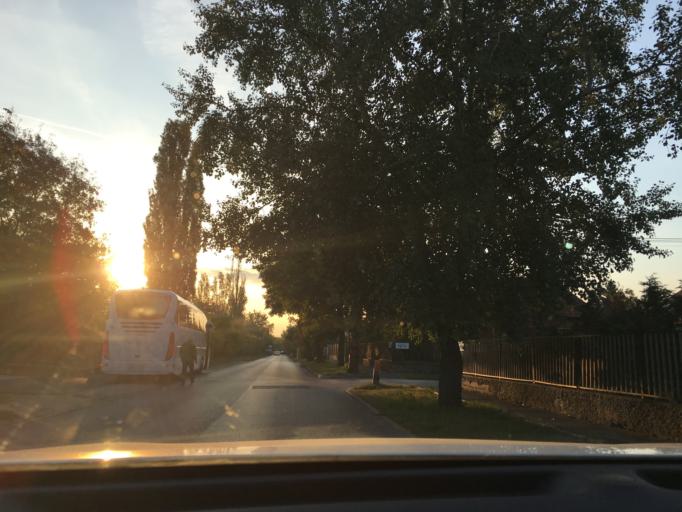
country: HU
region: Budapest
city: Budapest XVII. keruelet
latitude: 47.4758
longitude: 19.2493
